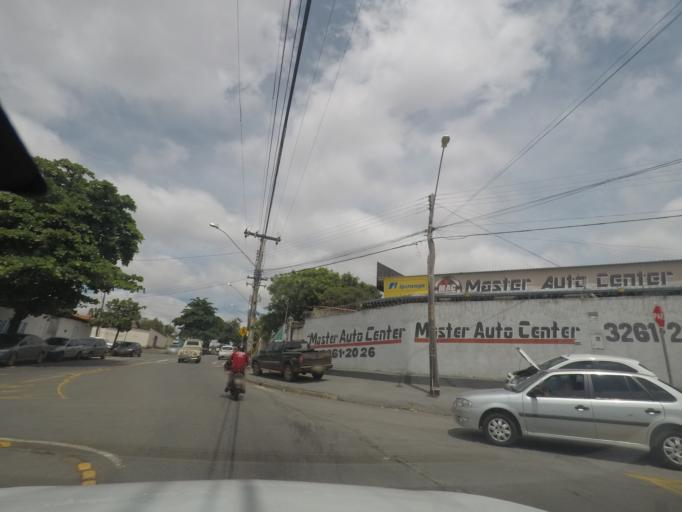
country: BR
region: Goias
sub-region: Goiania
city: Goiania
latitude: -16.6730
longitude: -49.2299
